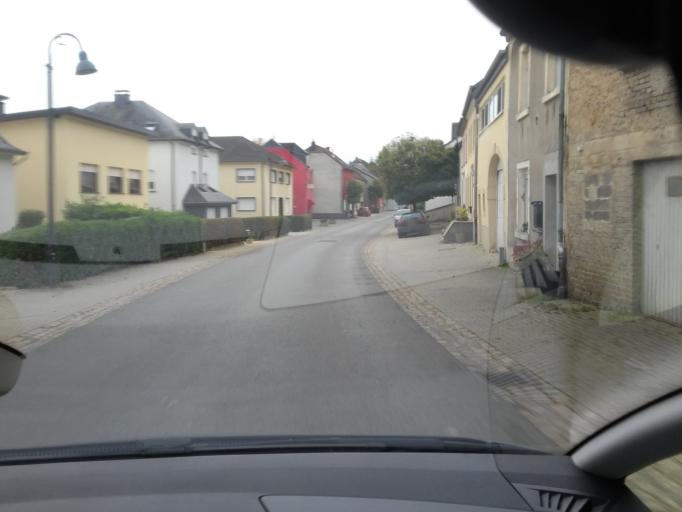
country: LU
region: Diekirch
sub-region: Canton de Redange
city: Beckerich
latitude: 49.7294
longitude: 5.8870
